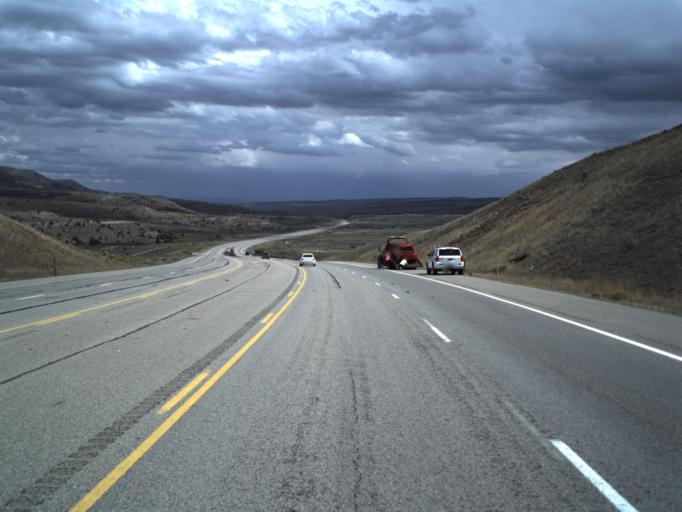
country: US
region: Utah
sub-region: Carbon County
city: Helper
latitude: 39.8454
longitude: -111.0023
